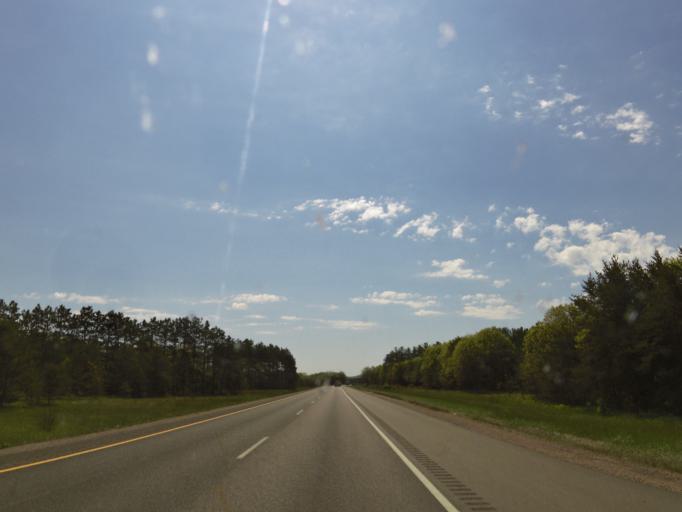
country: US
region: Wisconsin
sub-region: Trempealeau County
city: Osseo
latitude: 44.5504
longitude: -91.1678
